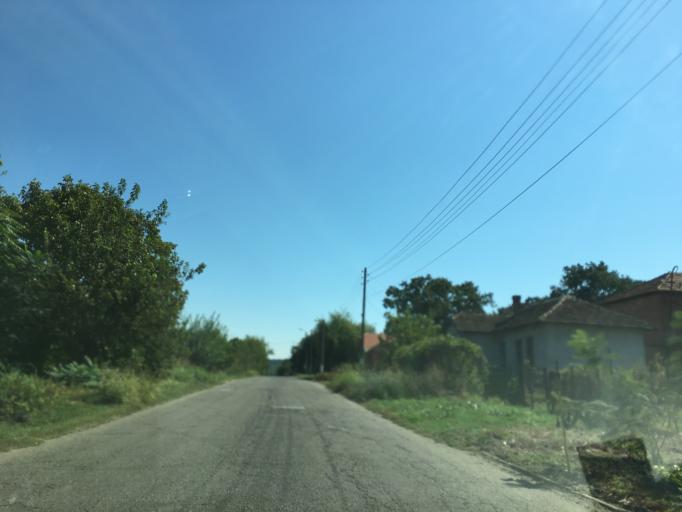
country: RO
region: Dolj
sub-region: Comuna Desa
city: Desa
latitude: 43.7681
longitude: 23.0059
